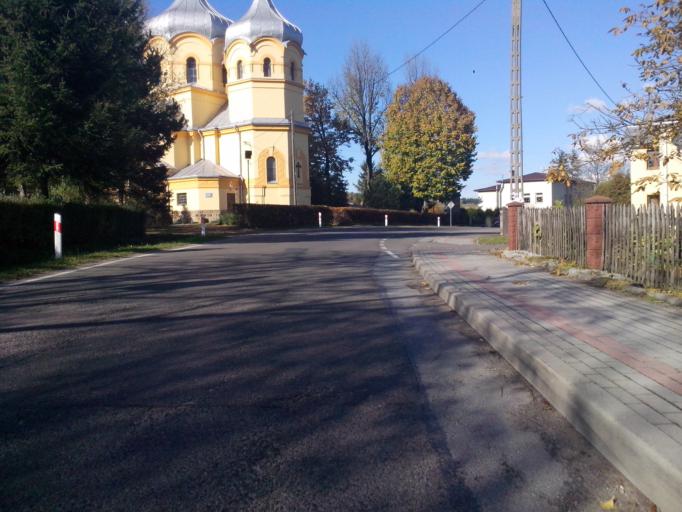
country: PL
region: Subcarpathian Voivodeship
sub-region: Powiat strzyzowski
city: Jawornik
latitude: 49.7800
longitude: 21.8544
